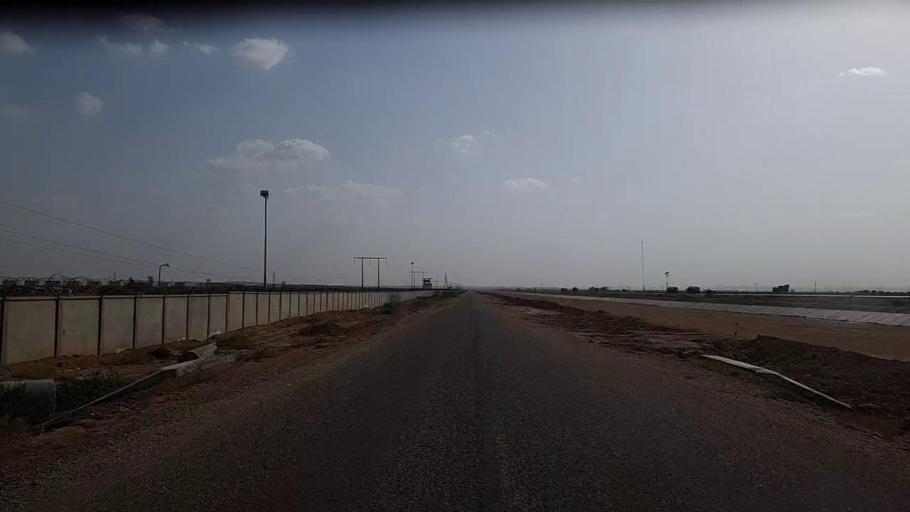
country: PK
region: Sindh
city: Kotri
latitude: 25.2828
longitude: 68.0325
